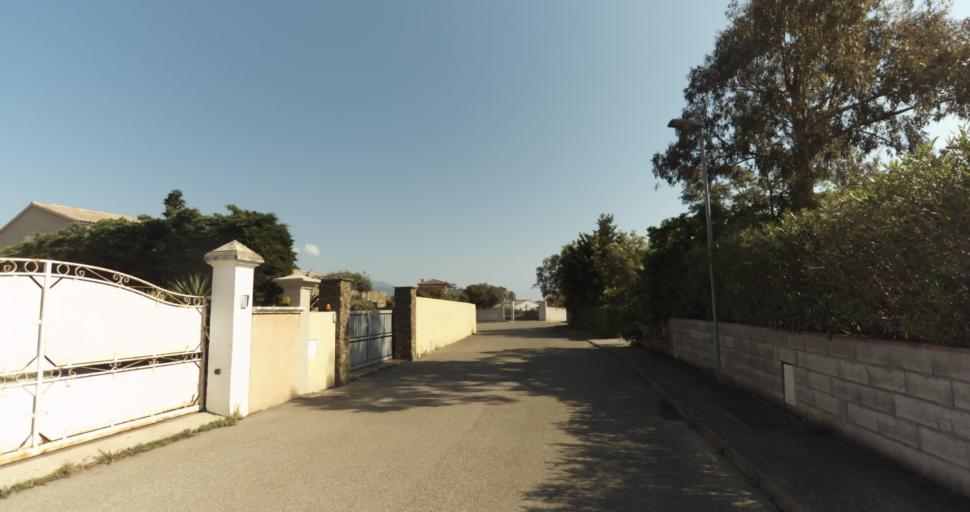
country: FR
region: Corsica
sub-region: Departement de la Haute-Corse
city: Biguglia
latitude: 42.6230
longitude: 9.4351
